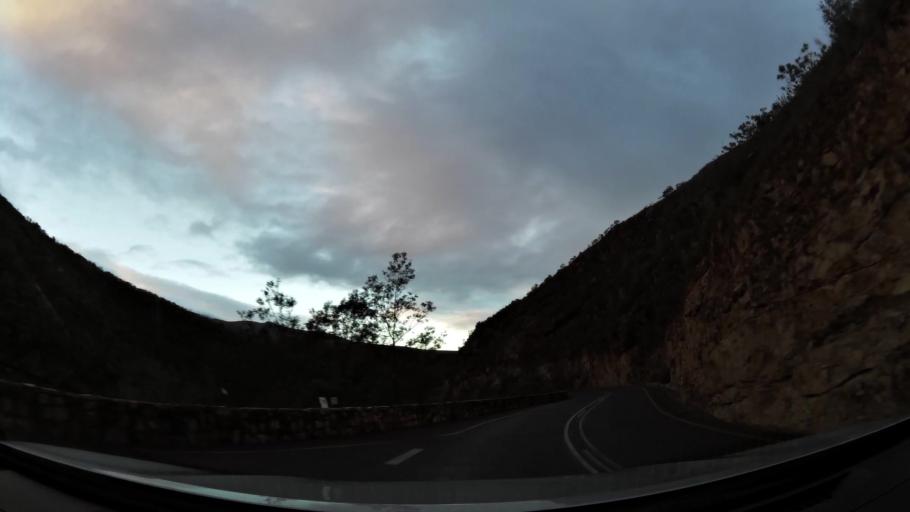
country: ZA
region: Western Cape
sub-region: Overberg District Municipality
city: Swellendam
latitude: -33.9892
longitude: 20.7107
